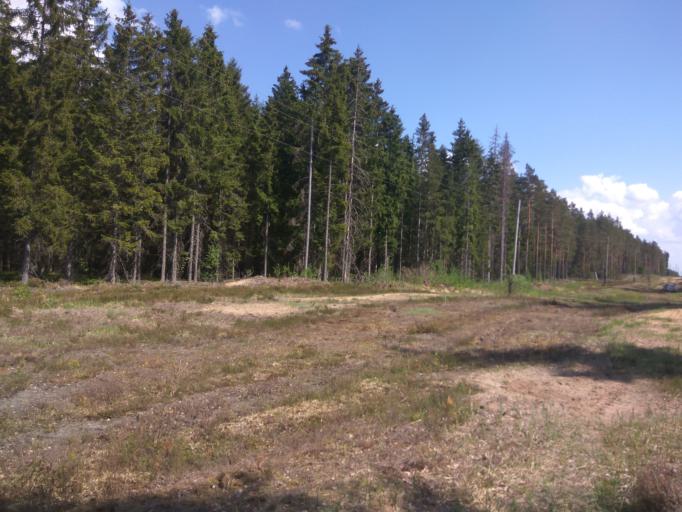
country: LV
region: Kuldigas Rajons
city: Kuldiga
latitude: 57.1842
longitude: 21.9950
